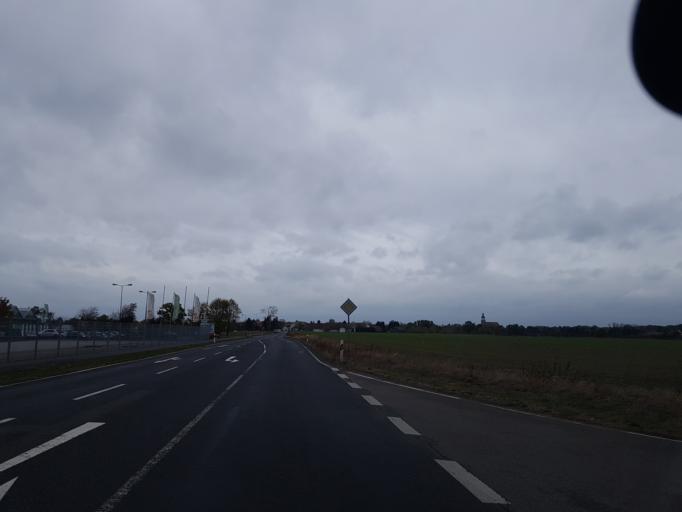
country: DE
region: Brandenburg
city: Herzberg
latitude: 51.6782
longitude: 13.2303
